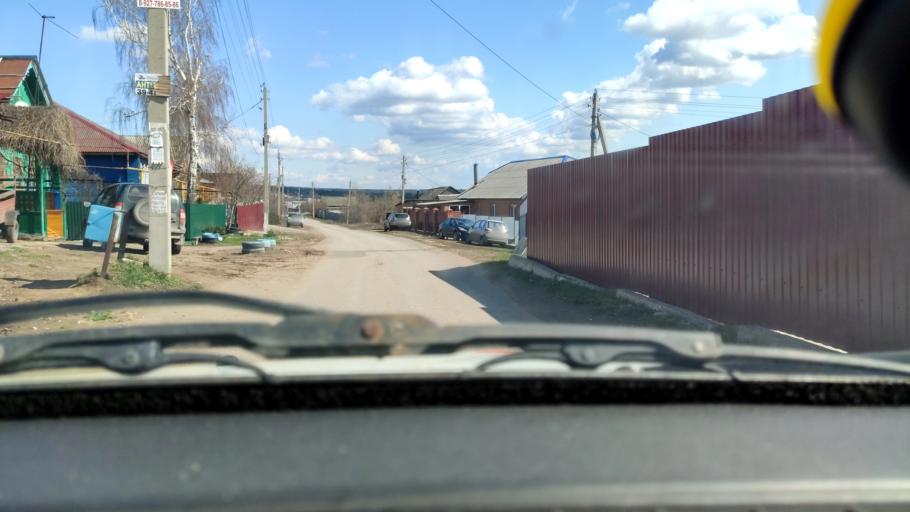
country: RU
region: Samara
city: Zhigulevsk
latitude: 53.5411
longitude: 49.5200
